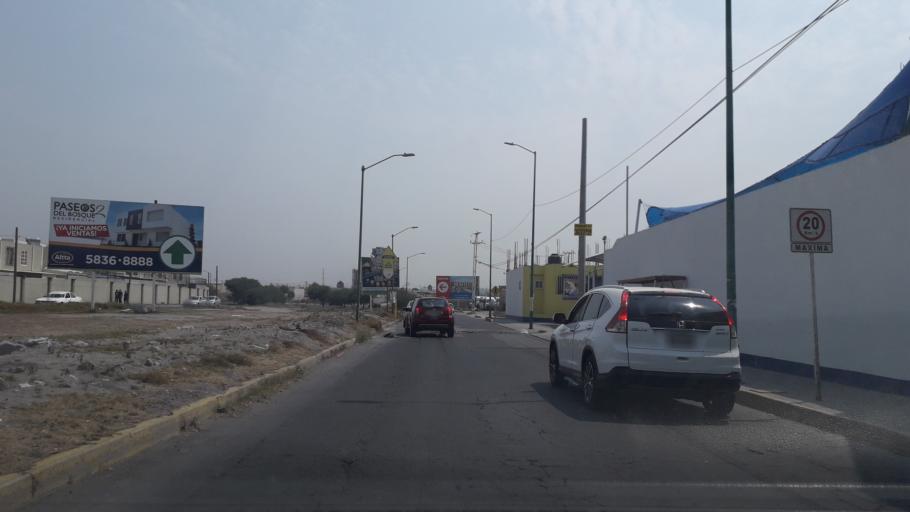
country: MX
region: Mexico
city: Santo Tomas Chiconautla
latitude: 19.6400
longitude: -99.0238
